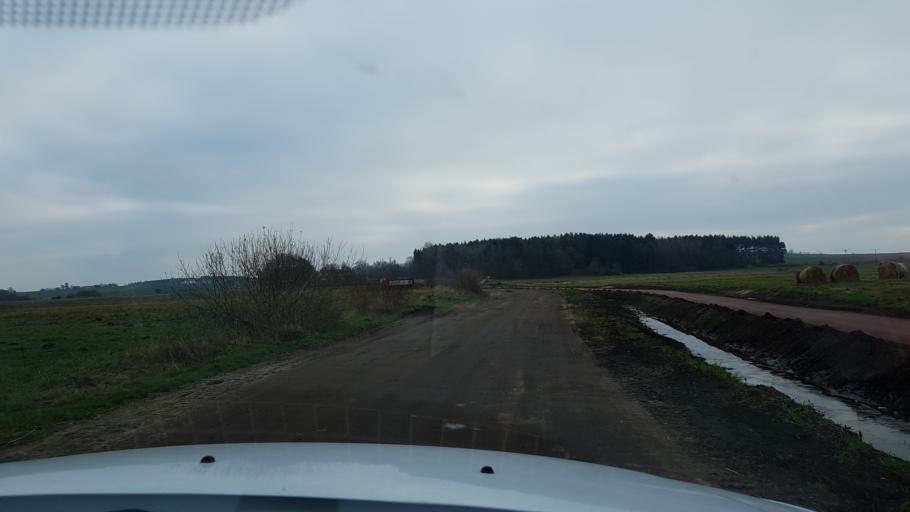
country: PL
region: West Pomeranian Voivodeship
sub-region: Powiat kolobrzeski
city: Grzybowo
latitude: 54.1283
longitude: 15.5158
